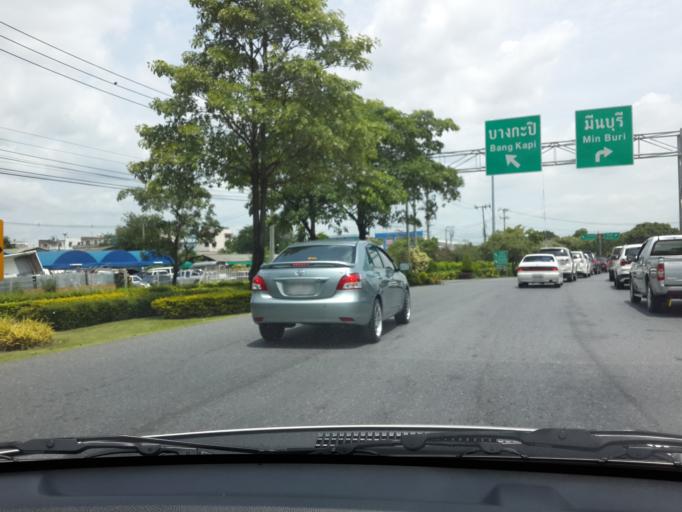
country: TH
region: Bangkok
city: Saphan Sung
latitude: 13.7814
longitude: 100.6831
